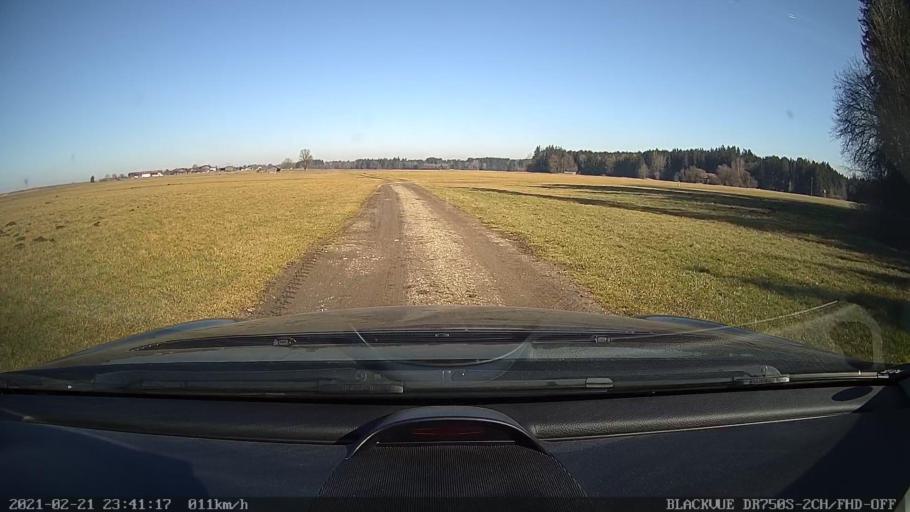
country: DE
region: Bavaria
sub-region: Upper Bavaria
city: Schonstett
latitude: 47.9934
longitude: 12.2147
